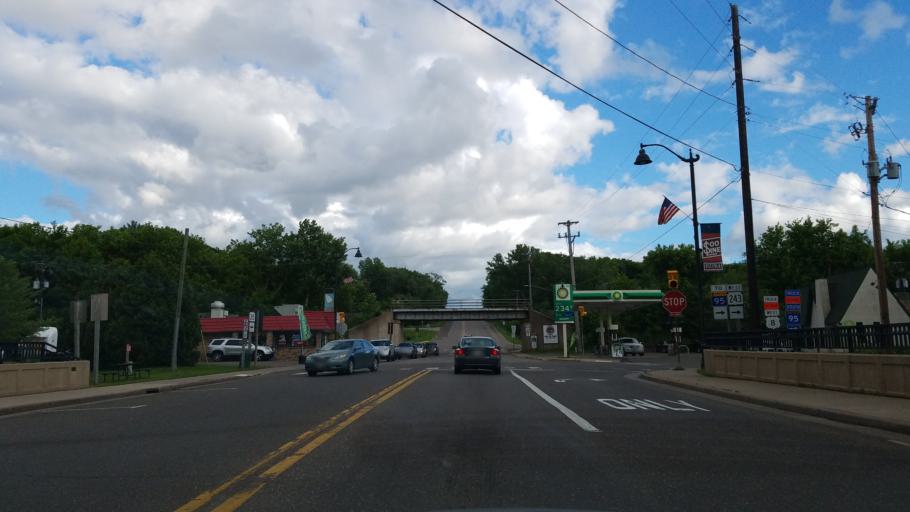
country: US
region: Wisconsin
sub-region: Polk County
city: Osceola
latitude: 45.3194
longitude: -92.7057
